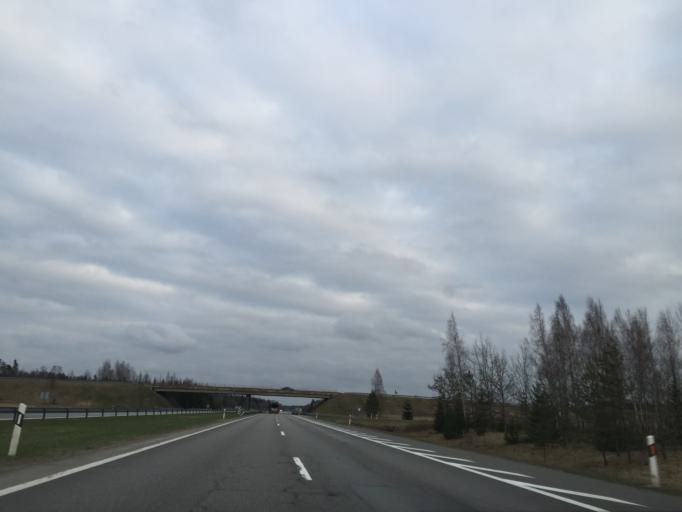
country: LT
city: Rietavas
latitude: 55.6271
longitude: 21.9724
